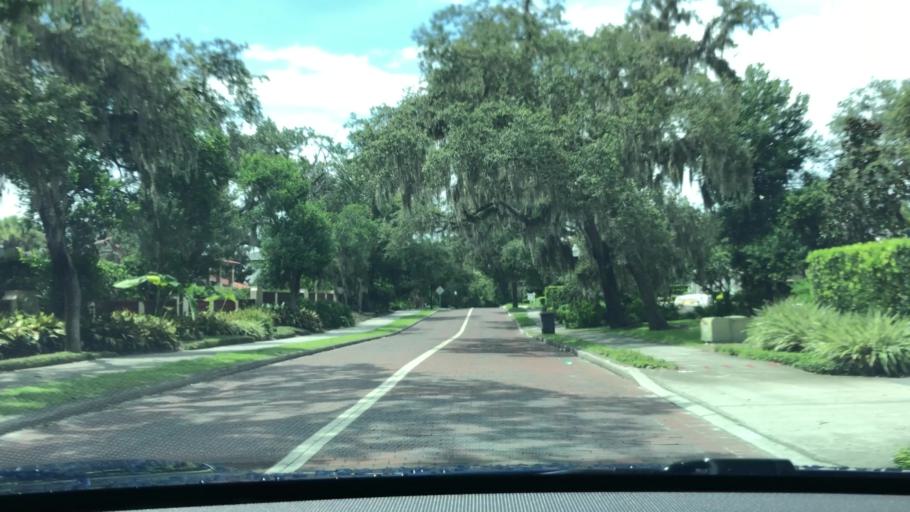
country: US
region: Florida
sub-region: Orange County
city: Winter Park
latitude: 28.5839
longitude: -81.3544
